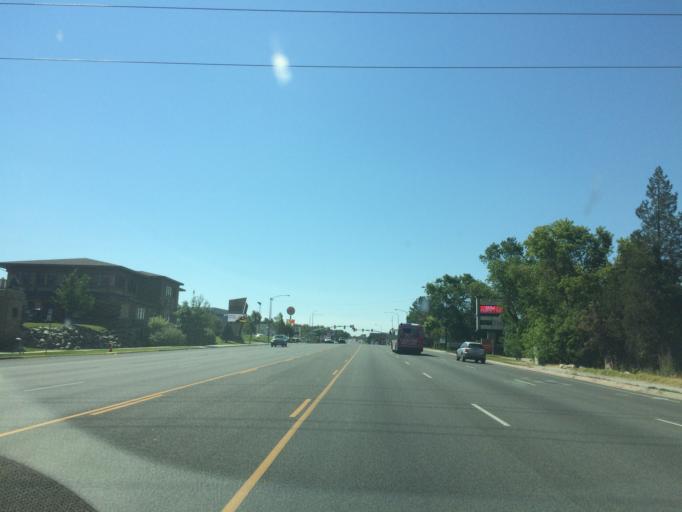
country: US
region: Utah
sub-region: Weber County
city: South Ogden
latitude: 41.1886
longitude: -111.9490
